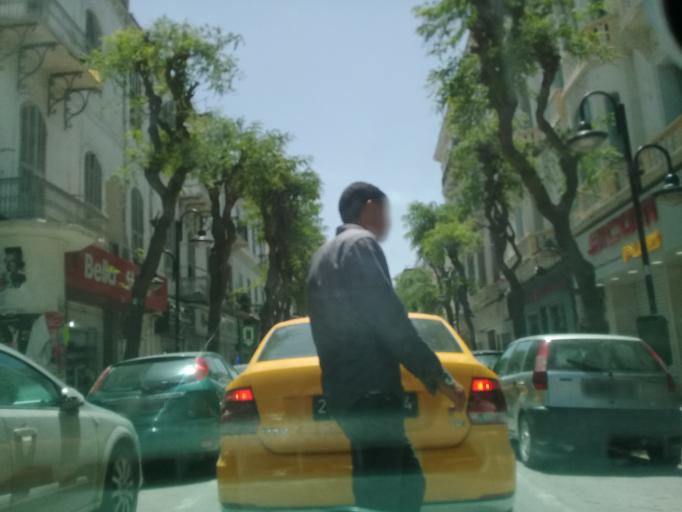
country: TN
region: Tunis
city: Tunis
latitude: 36.7981
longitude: 10.1787
